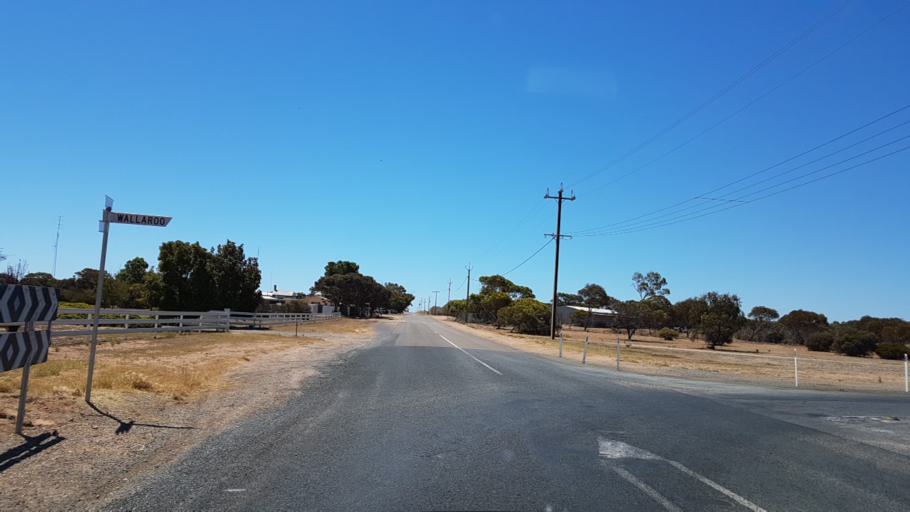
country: AU
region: South Australia
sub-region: Copper Coast
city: Wallaroo
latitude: -34.0529
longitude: 137.5930
